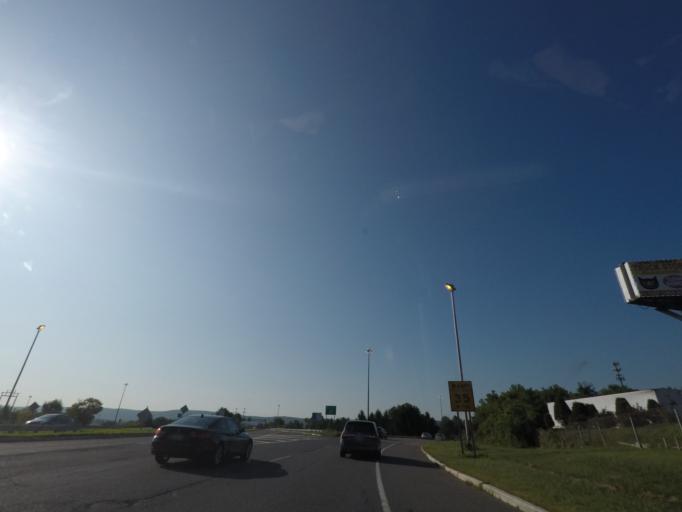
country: US
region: New Jersey
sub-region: Warren County
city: Alpha
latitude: 40.6724
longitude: -75.1379
